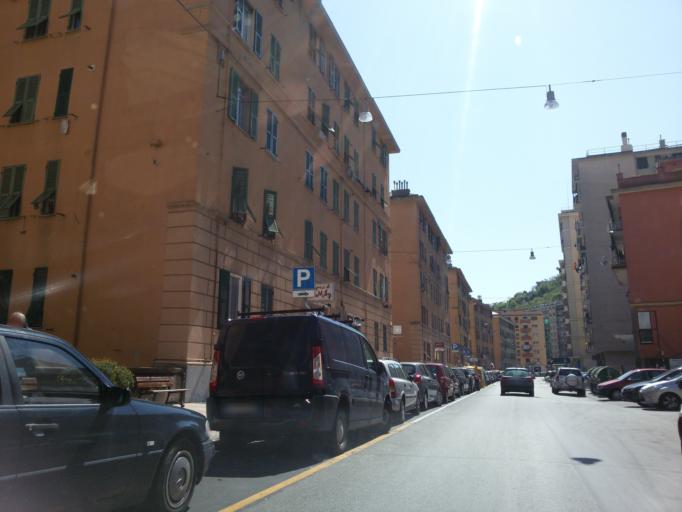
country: IT
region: Liguria
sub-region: Provincia di Genova
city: Piccarello
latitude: 44.4453
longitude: 8.9659
